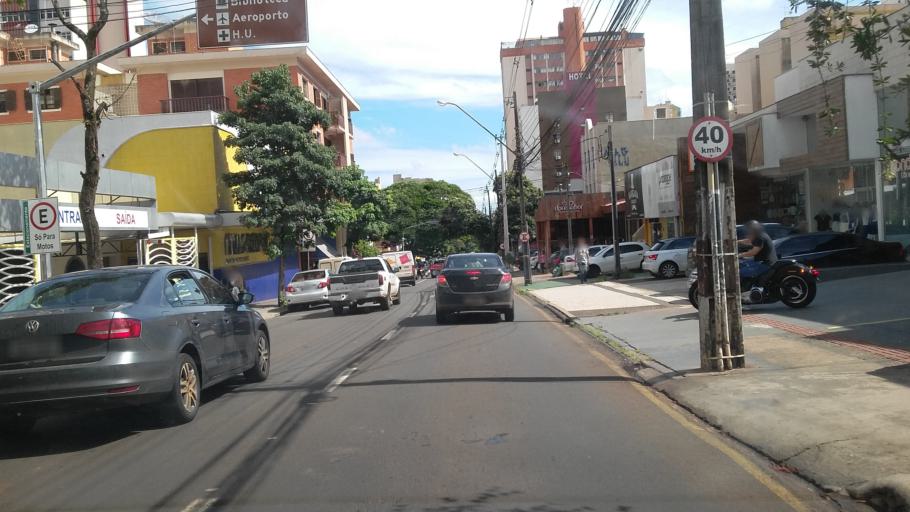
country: BR
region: Parana
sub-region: Londrina
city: Londrina
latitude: -23.3147
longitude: -51.1628
